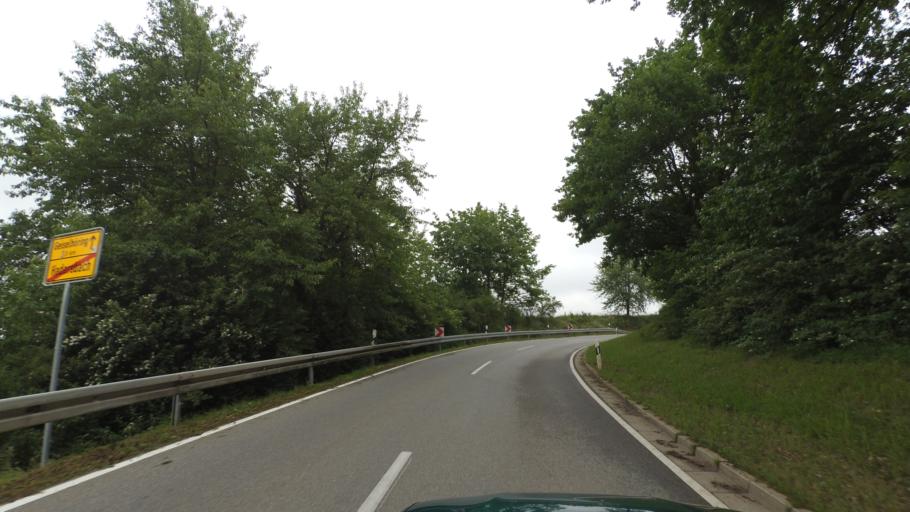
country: DE
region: Bavaria
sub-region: Lower Bavaria
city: Geiselhoring
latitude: 48.8030
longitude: 12.3812
